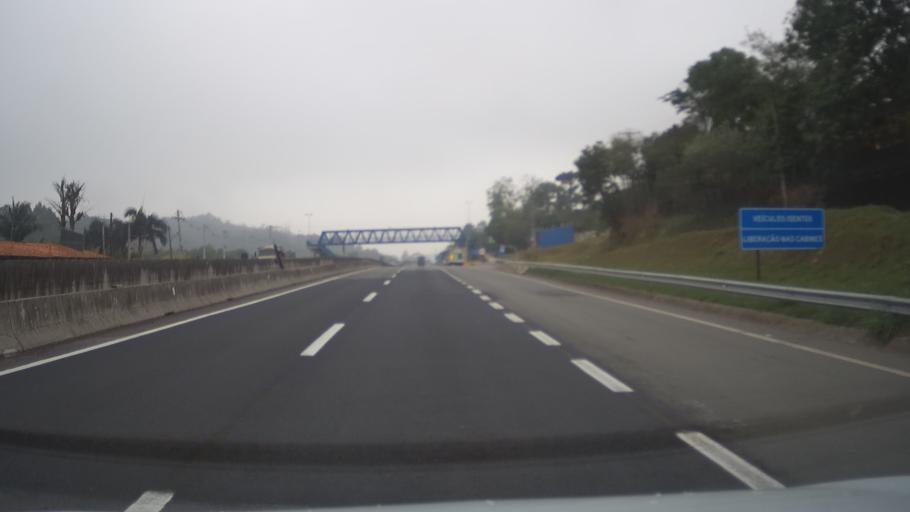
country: BR
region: Sao Paulo
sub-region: Itatiba
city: Itatiba
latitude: -23.0841
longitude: -46.8462
